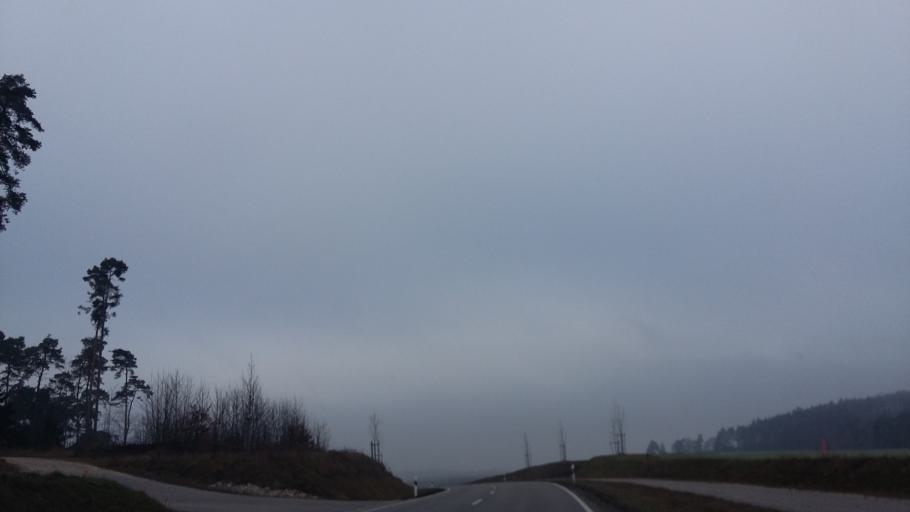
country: DE
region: Bavaria
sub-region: Swabia
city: Pottmes
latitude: 48.5570
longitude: 11.1103
